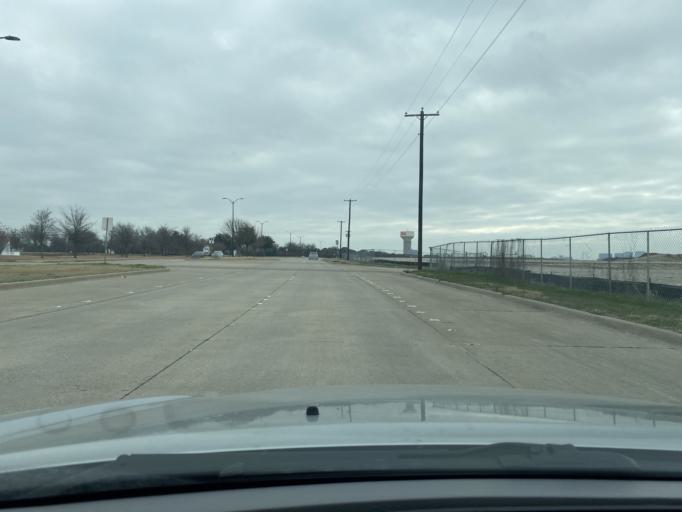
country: US
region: Texas
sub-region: Collin County
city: Frisco
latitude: 33.1205
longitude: -96.8161
